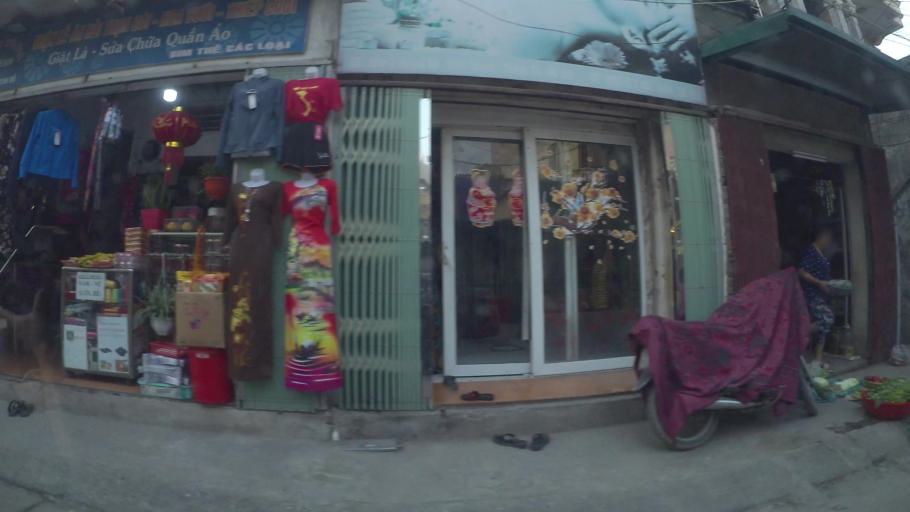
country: VN
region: Ha Noi
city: Van Dien
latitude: 20.9378
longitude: 105.8393
